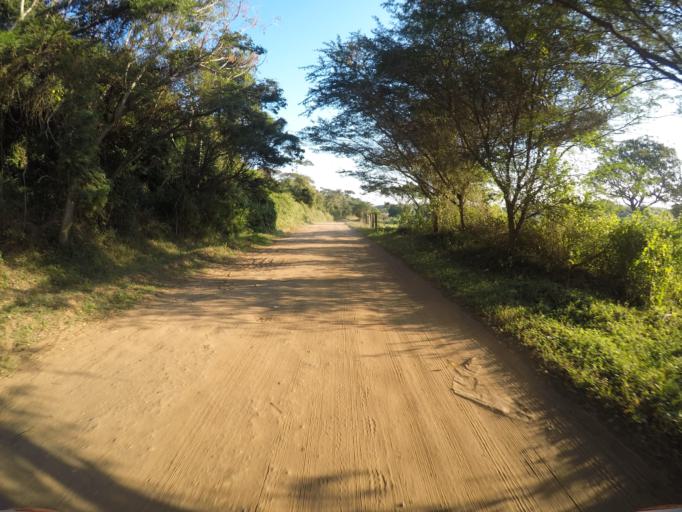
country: ZA
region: KwaZulu-Natal
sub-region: uThungulu District Municipality
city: KwaMbonambi
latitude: -28.7035
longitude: 32.1892
